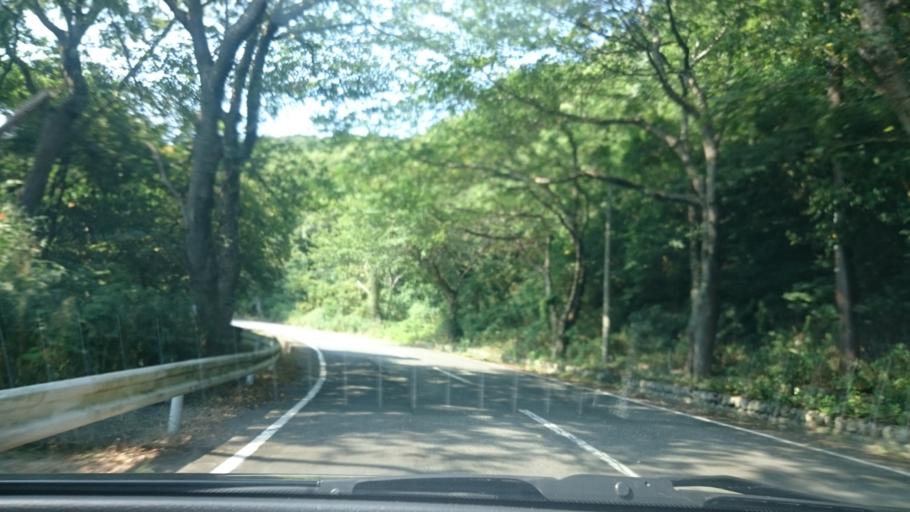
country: JP
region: Shizuoka
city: Heda
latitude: 34.9817
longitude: 138.7732
